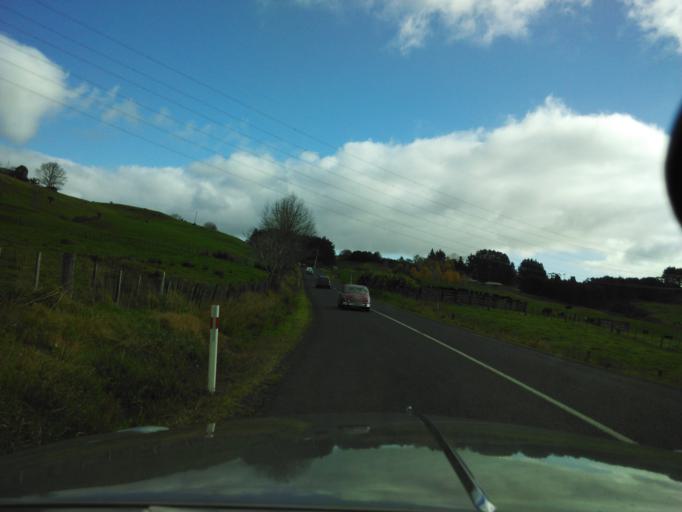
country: NZ
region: Auckland
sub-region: Auckland
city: Red Hill
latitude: -37.0840
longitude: 175.0824
